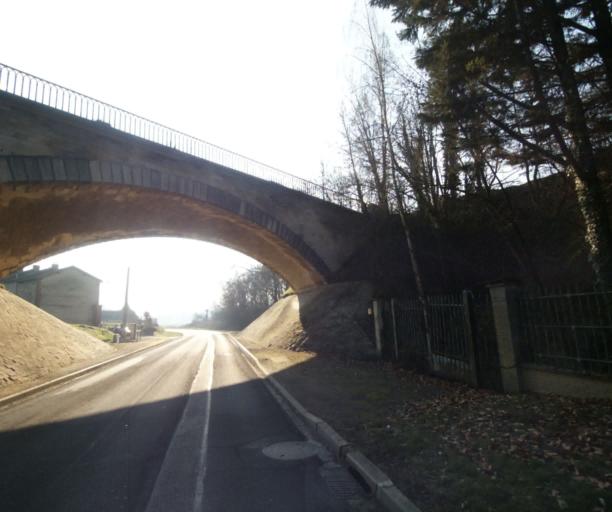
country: FR
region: Champagne-Ardenne
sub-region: Departement de la Haute-Marne
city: Wassy
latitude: 48.4862
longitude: 4.9685
